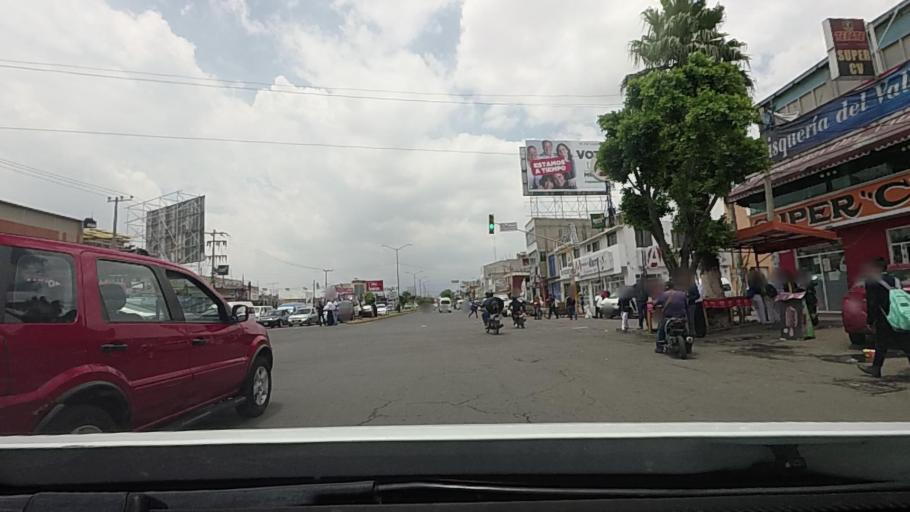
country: MX
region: Mexico
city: Chalco de Diaz Covarrubias
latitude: 19.2657
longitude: -98.8976
